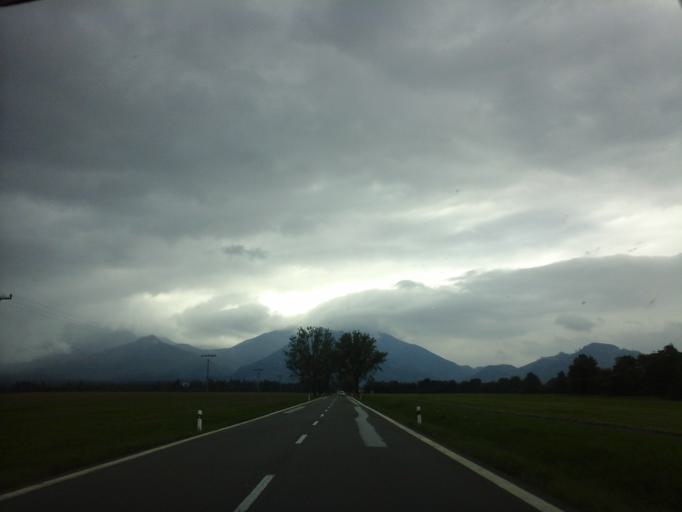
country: SK
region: Presovsky
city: Spisska Bela
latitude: 49.2061
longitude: 20.3930
